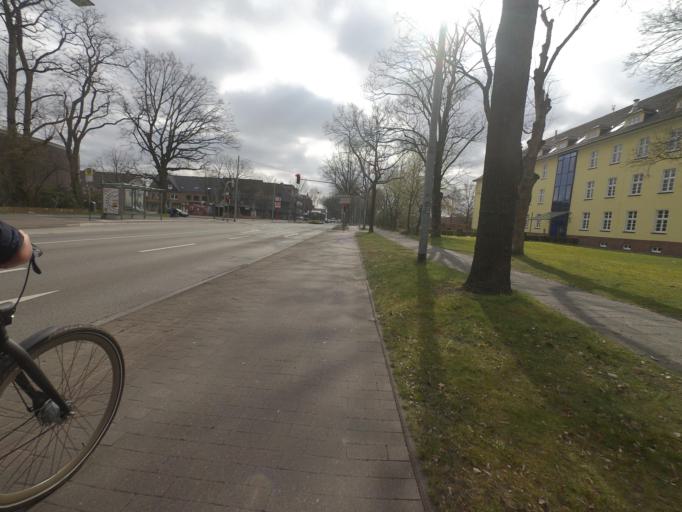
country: DE
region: Lower Saxony
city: Oldenburg
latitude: 53.1099
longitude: 8.2093
